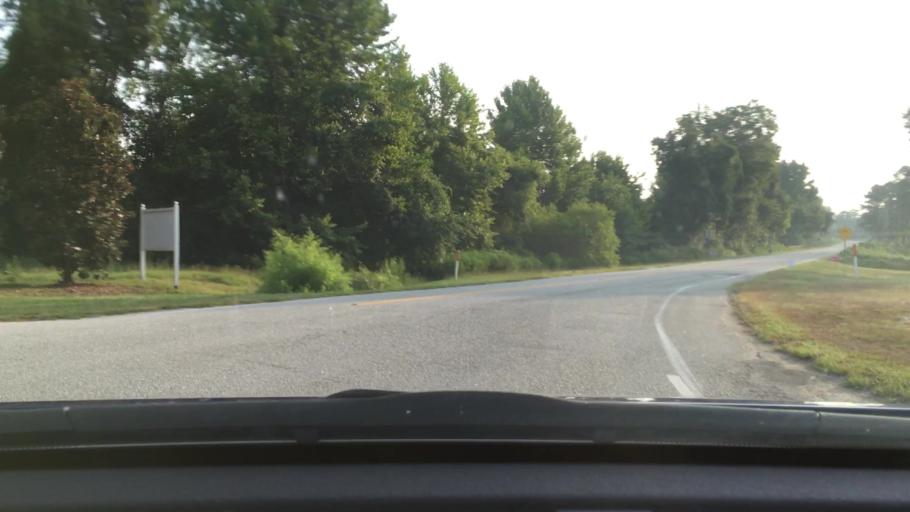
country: US
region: South Carolina
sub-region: Florence County
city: Timmonsville
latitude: 34.1763
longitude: -80.0585
